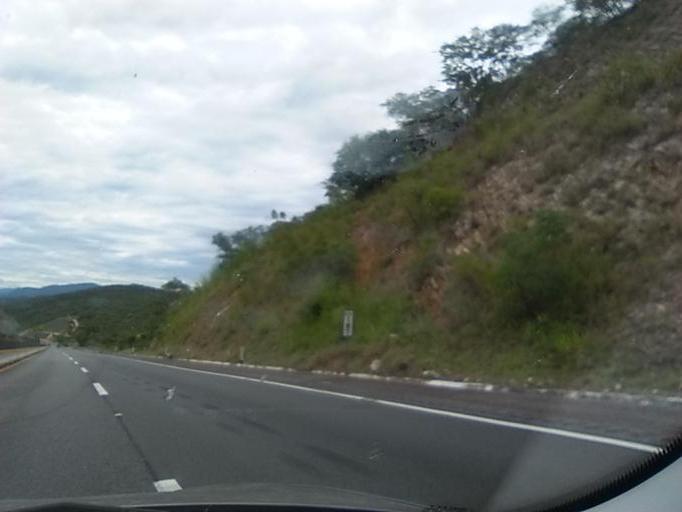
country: MX
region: Guerrero
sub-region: Huitzuco de los Figueroa
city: Ciudad de Huitzuco
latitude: 18.1554
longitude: -99.2130
